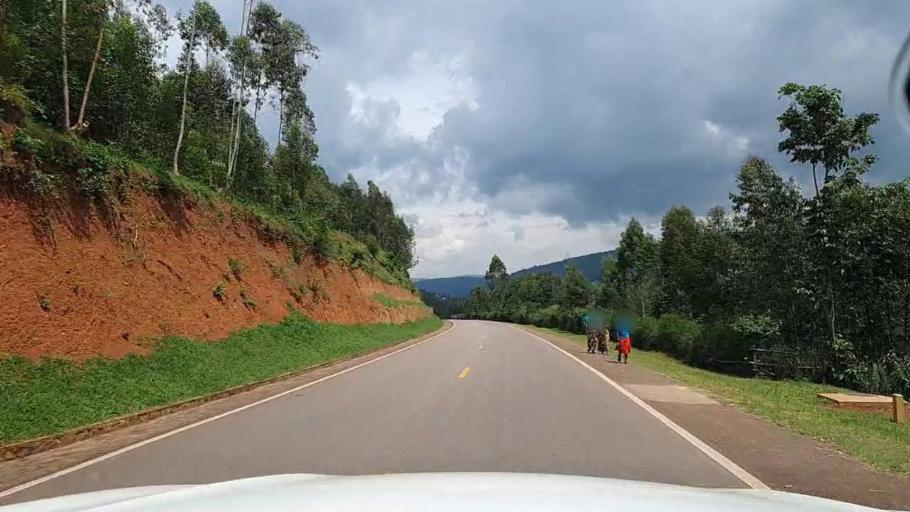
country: RW
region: Kigali
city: Kigali
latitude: -1.7989
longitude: 30.1289
